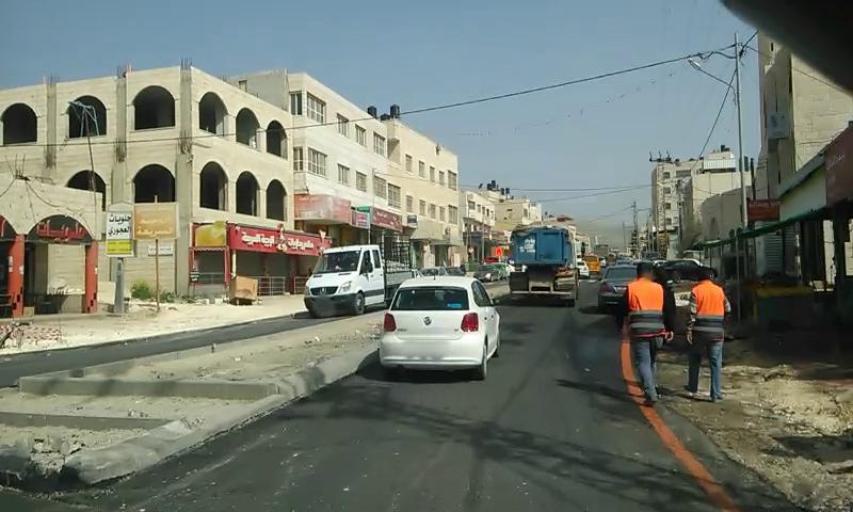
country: PS
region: West Bank
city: Huwwarah
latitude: 32.1491
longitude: 35.2580
